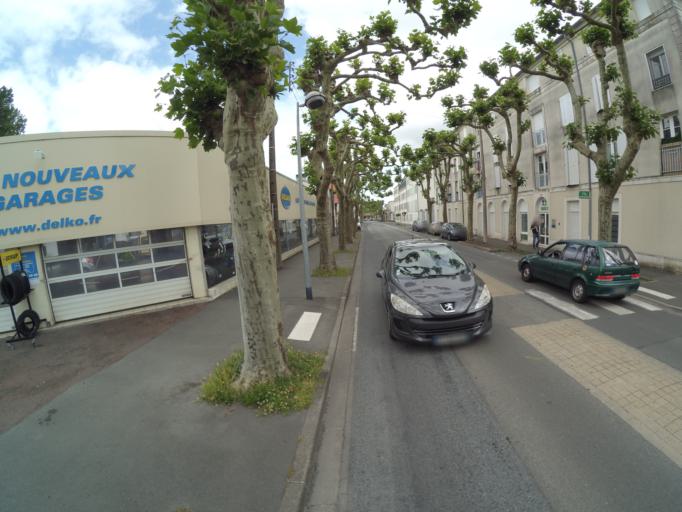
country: FR
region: Poitou-Charentes
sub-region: Departement de la Charente-Maritime
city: Rochefort
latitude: 45.9446
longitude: -0.9617
